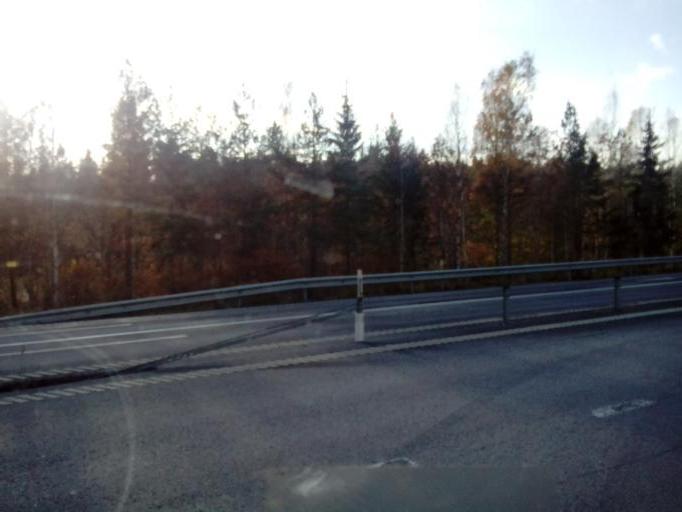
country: SE
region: Kalmar
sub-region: Vimmerby Kommun
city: Vimmerby
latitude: 57.7175
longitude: 16.0667
